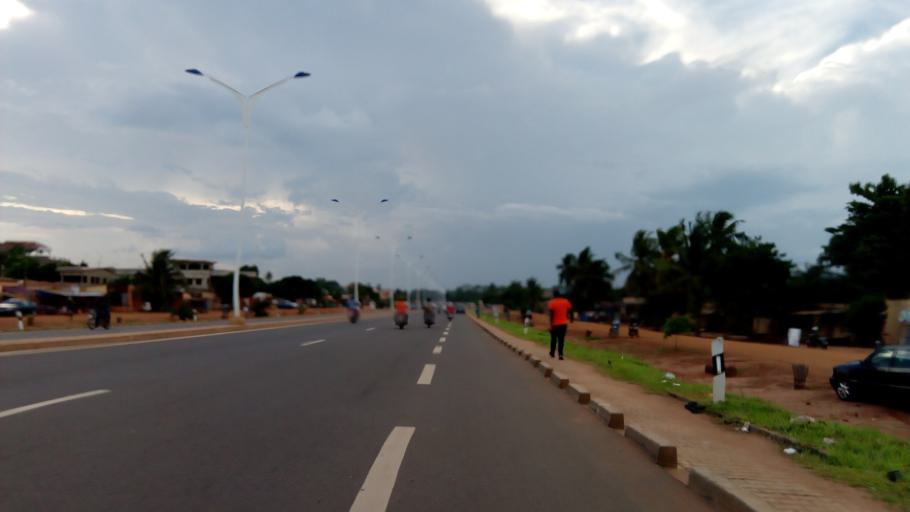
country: TG
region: Maritime
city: Lome
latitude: 6.2430
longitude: 1.1972
